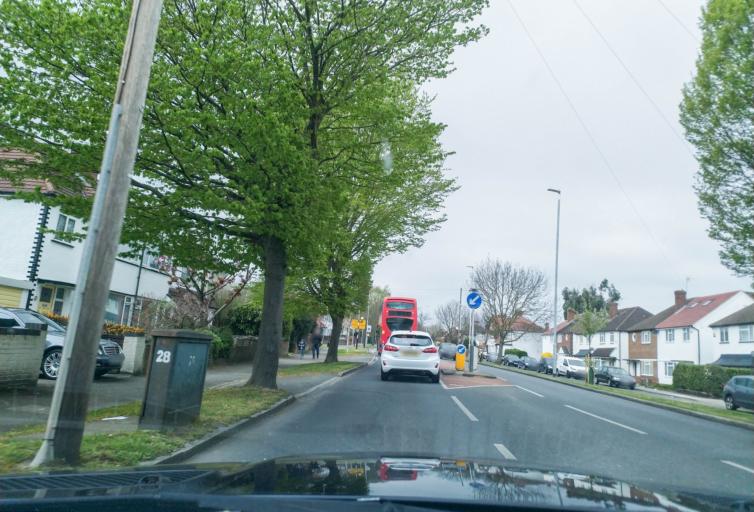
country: GB
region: England
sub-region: Greater London
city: Pinner
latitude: 51.5713
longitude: -0.3920
